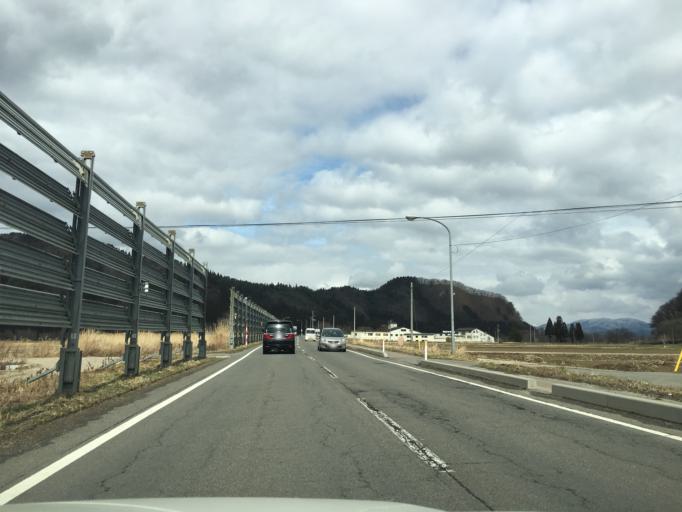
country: JP
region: Akita
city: Hanawa
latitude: 40.2400
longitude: 140.7382
